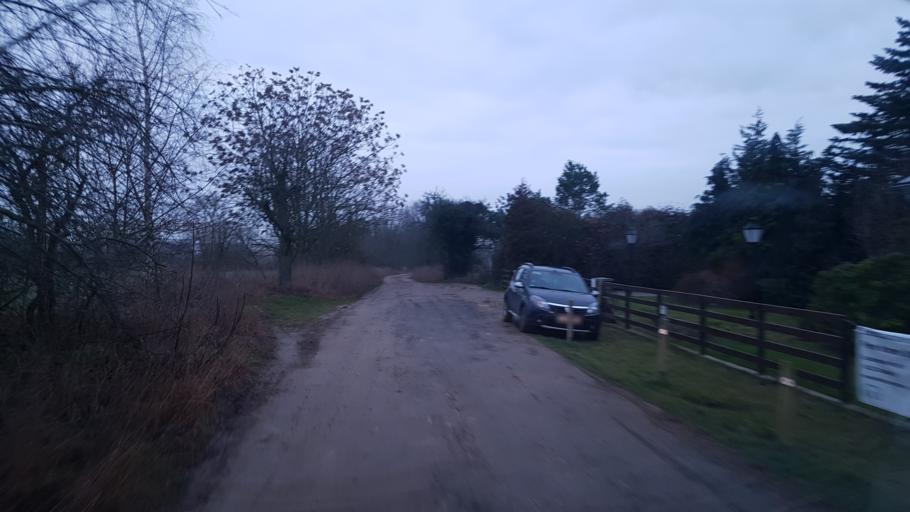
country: DE
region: Brandenburg
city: Stahnsdorf
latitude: 52.3632
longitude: 13.1983
